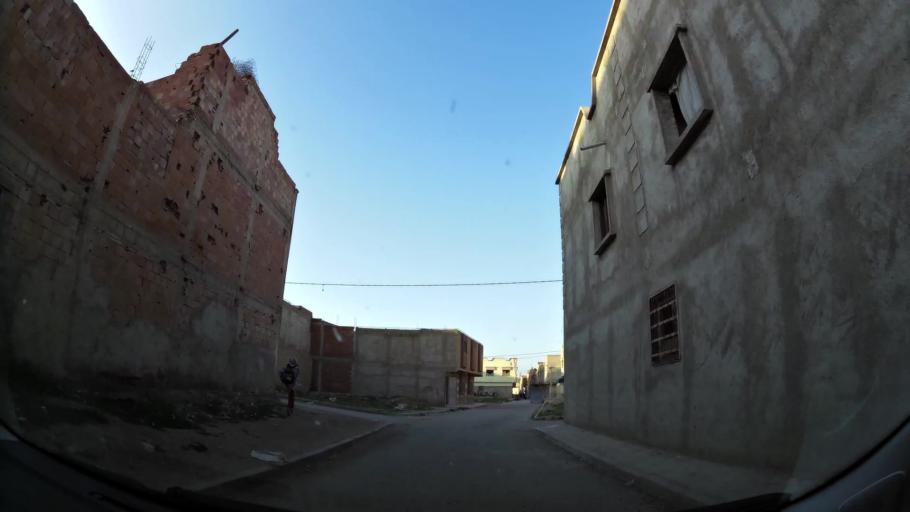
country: MA
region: Oriental
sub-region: Oujda-Angad
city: Oujda
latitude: 34.7108
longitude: -1.9069
